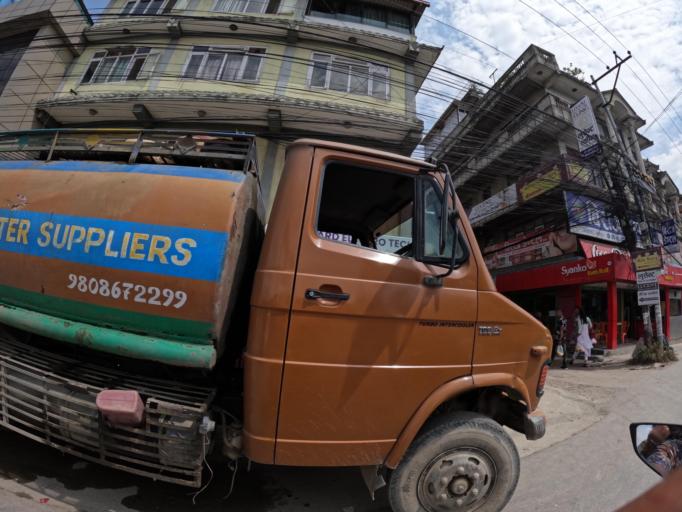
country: NP
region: Central Region
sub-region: Bagmati Zone
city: Bhaktapur
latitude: 27.6742
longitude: 85.3724
